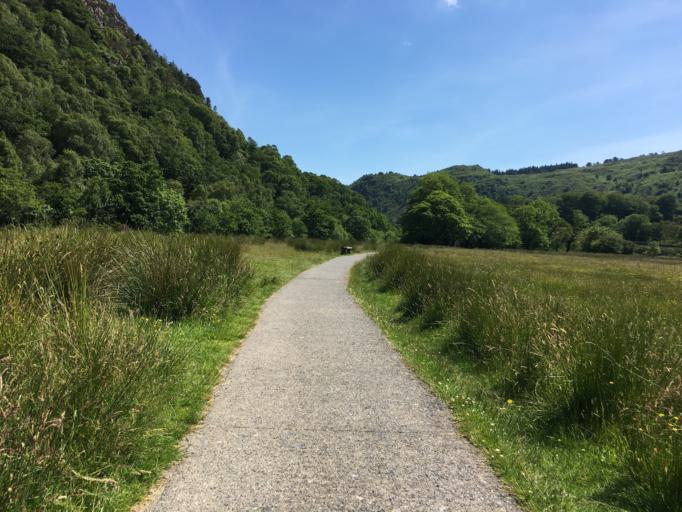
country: GB
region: Wales
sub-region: Gwynedd
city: Penrhyndeudraeth
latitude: 53.0082
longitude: -4.1004
